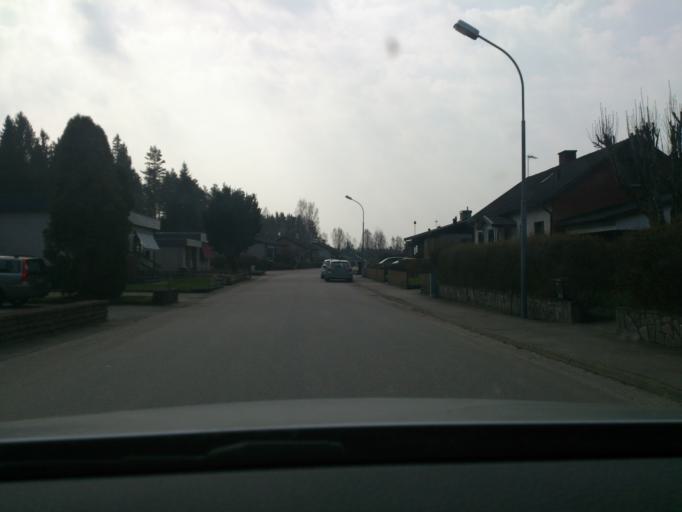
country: SE
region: Kronoberg
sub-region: Alvesta Kommun
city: Moheda
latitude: 57.0001
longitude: 14.5844
